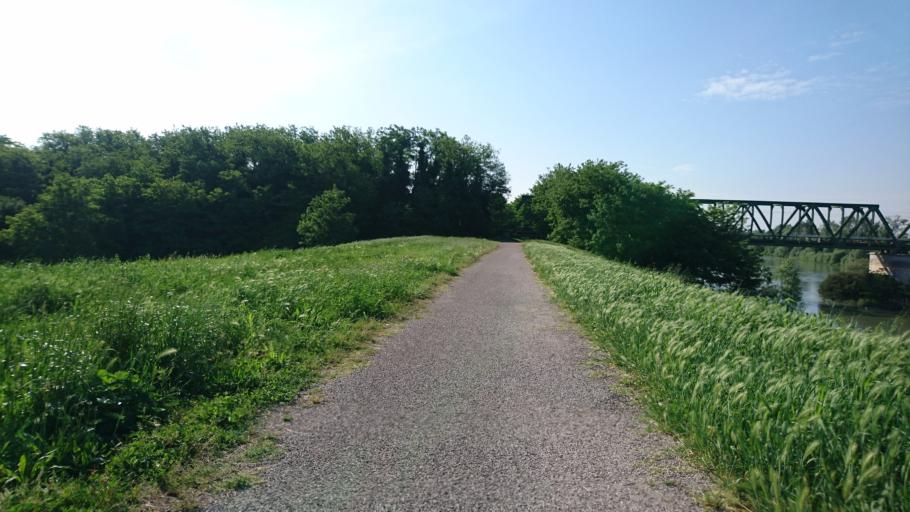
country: IT
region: Veneto
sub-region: Provincia di Verona
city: Boschi Sant'Anna
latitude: 45.1920
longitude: 11.3167
